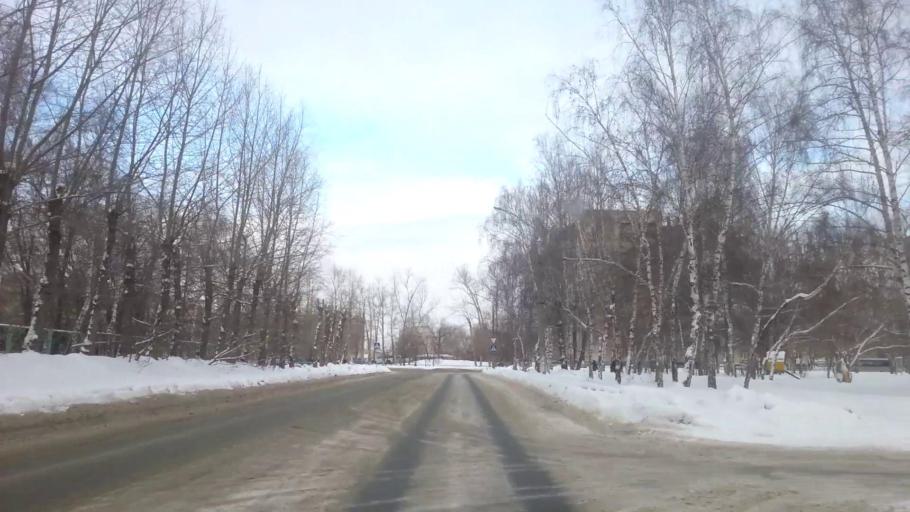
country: RU
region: Altai Krai
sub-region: Gorod Barnaulskiy
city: Barnaul
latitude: 53.3689
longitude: 83.6937
